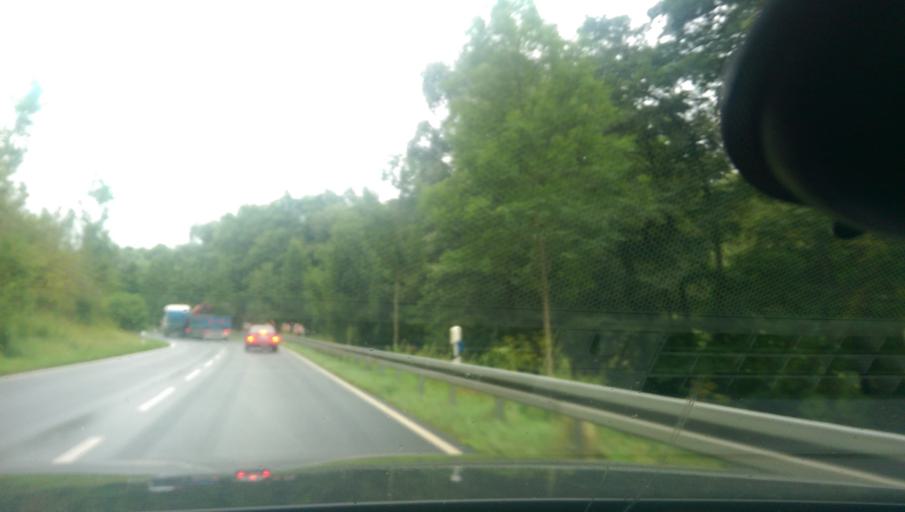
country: DE
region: Hesse
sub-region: Regierungsbezirk Kassel
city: Grossalmerode
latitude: 51.2572
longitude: 9.8309
